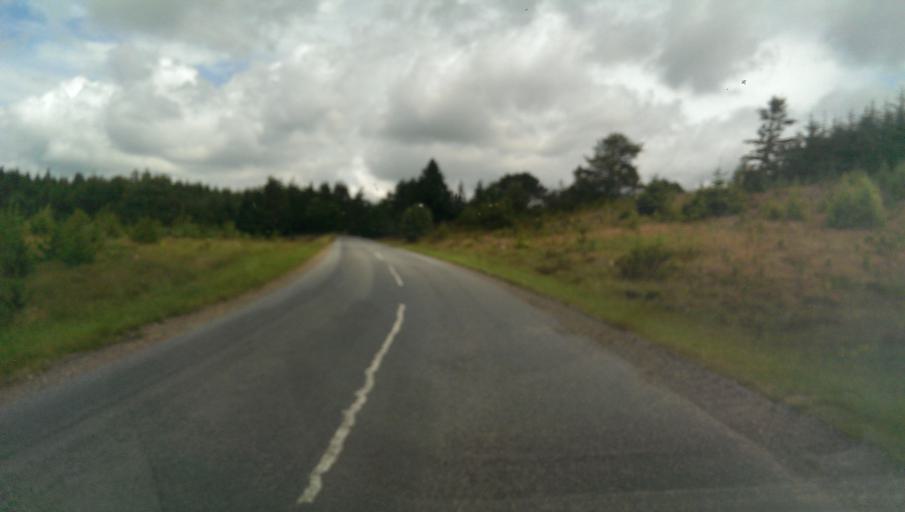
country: DK
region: Central Jutland
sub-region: Silkeborg Kommune
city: Virklund
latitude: 56.0859
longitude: 9.4286
